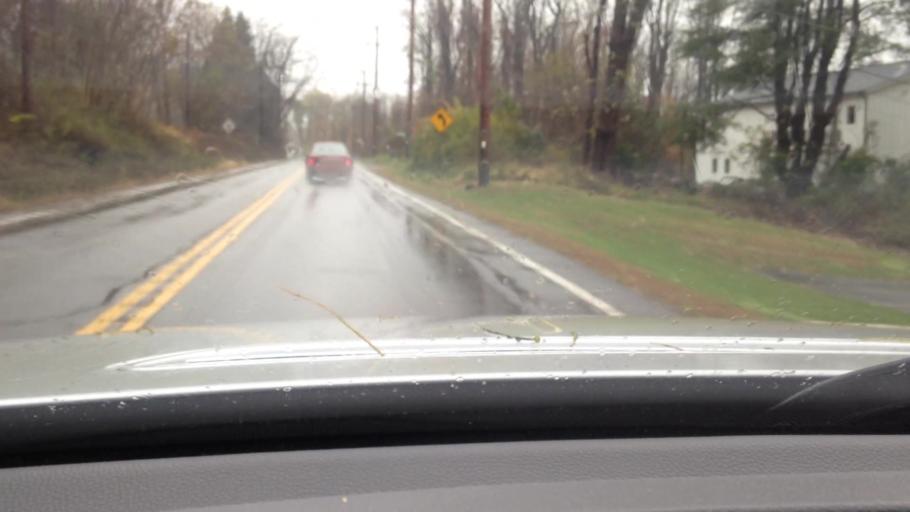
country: US
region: New York
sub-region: Dutchess County
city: Beacon
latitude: 41.4795
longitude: -73.9722
